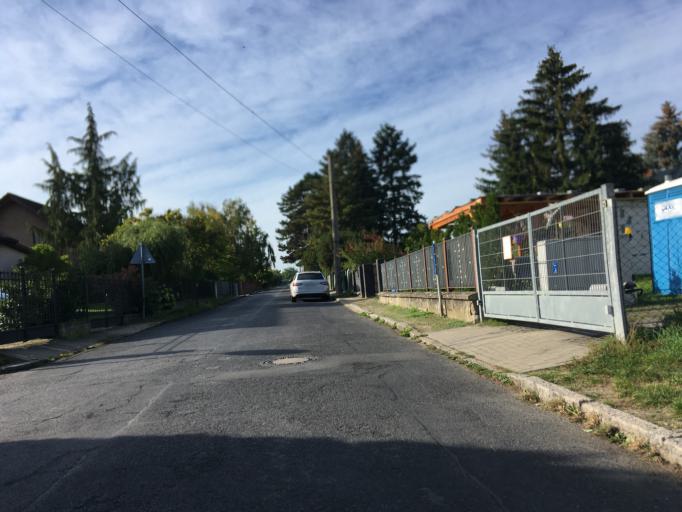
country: DE
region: Brandenburg
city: Hoppegarten
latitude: 52.5192
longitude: 13.6558
